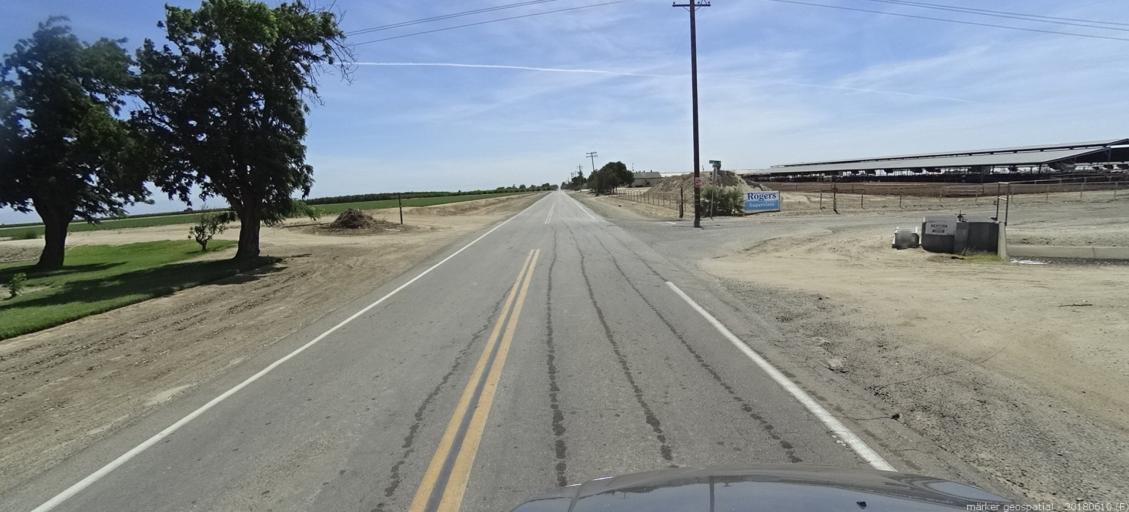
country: US
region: California
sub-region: Madera County
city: Chowchilla
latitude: 37.0181
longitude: -120.3470
